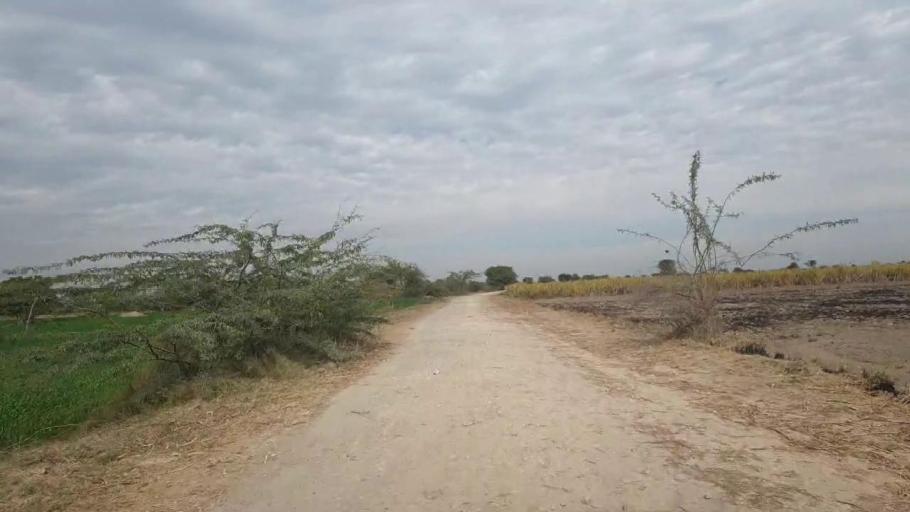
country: PK
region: Sindh
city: Jhol
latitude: 26.0127
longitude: 68.8725
